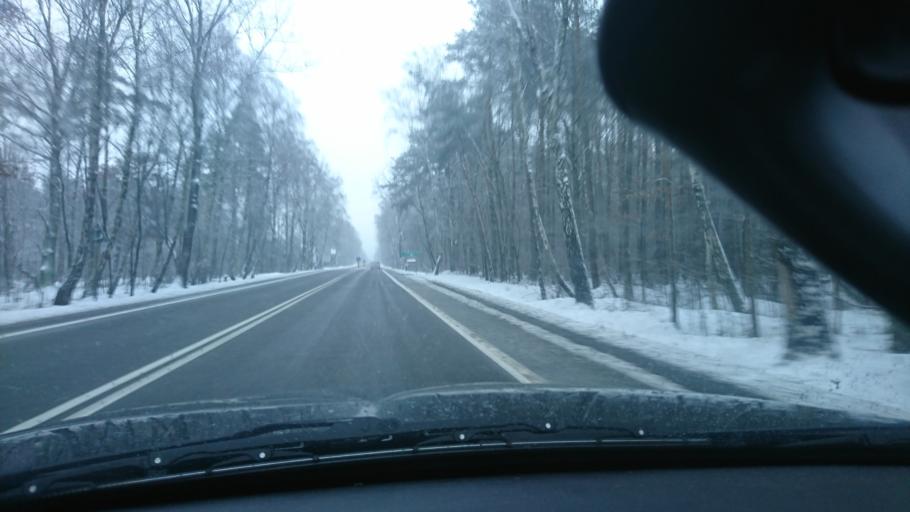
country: PL
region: Masovian Voivodeship
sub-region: Powiat ciechanowski
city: Glinojeck
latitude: 52.8327
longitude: 20.2640
